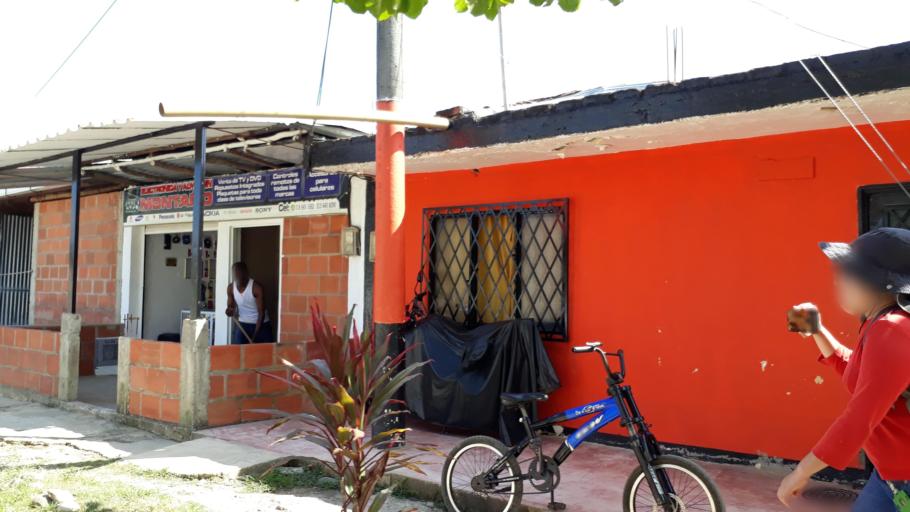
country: CO
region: Cauca
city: Buenos Aires
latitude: 3.1221
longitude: -76.6219
